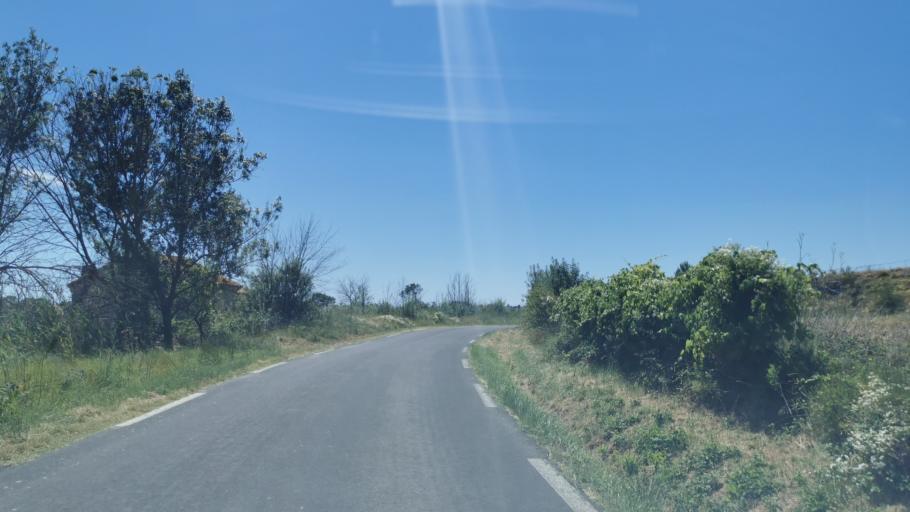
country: FR
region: Languedoc-Roussillon
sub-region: Departement de l'Herault
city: Nissan-lez-Enserune
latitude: 43.2668
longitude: 3.1229
